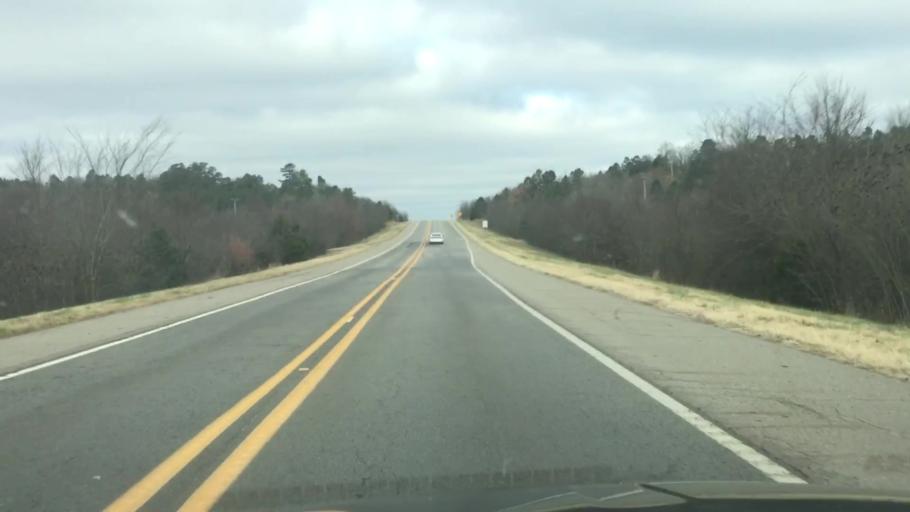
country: US
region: Arkansas
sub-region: Scott County
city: Waldron
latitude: 34.8589
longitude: -94.0694
